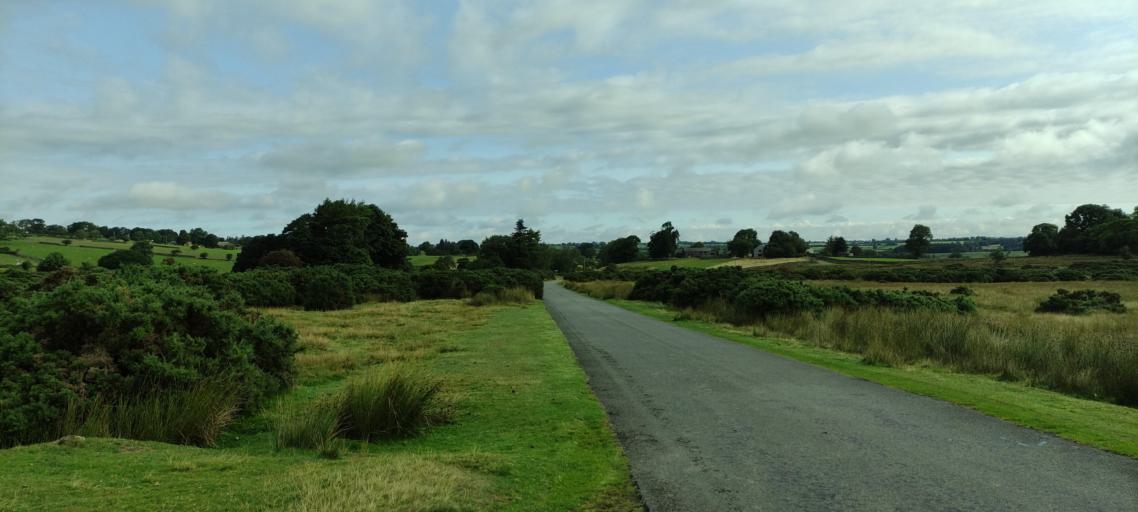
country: GB
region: England
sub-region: Cumbria
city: Keswick
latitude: 54.7072
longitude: -3.0027
